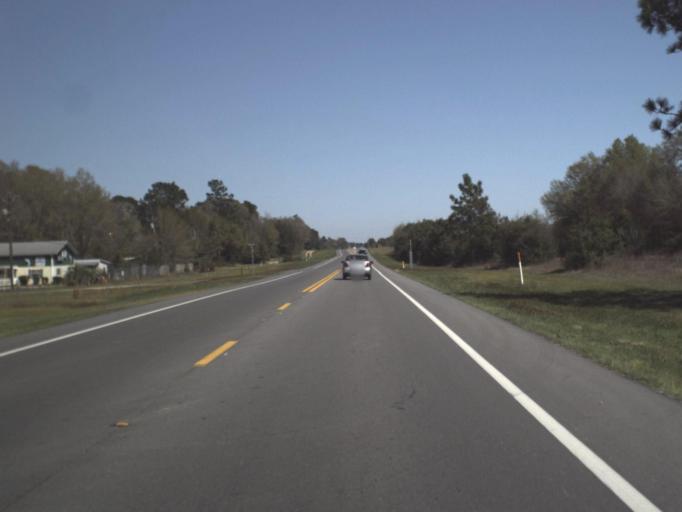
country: US
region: Florida
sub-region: Walton County
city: DeFuniak Springs
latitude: 30.7388
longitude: -86.1753
